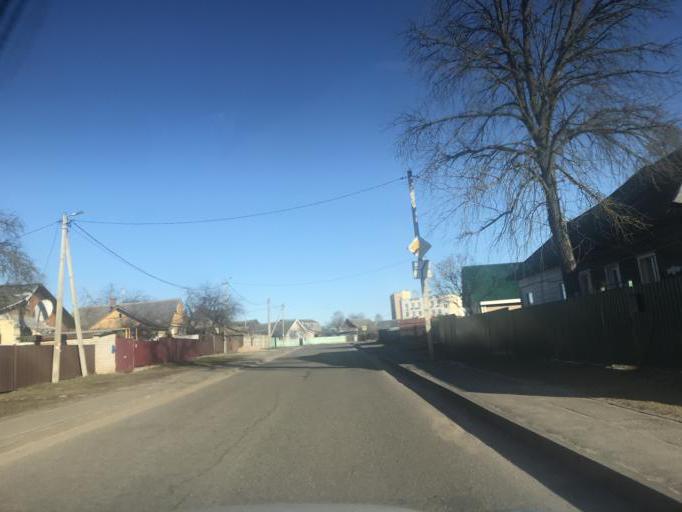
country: BY
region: Mogilev
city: Mahilyow
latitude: 53.9104
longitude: 30.3545
